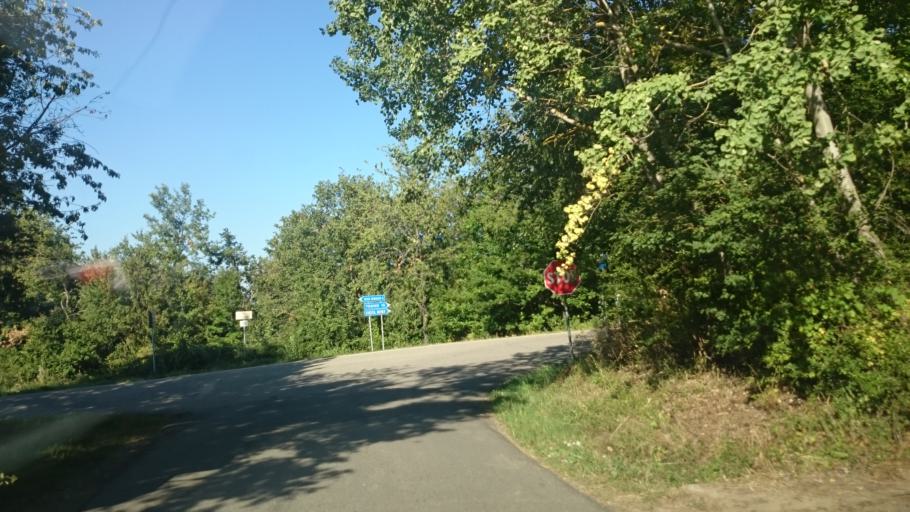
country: IT
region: Emilia-Romagna
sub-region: Provincia di Reggio Emilia
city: Villa Minozzo
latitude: 44.3483
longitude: 10.4847
